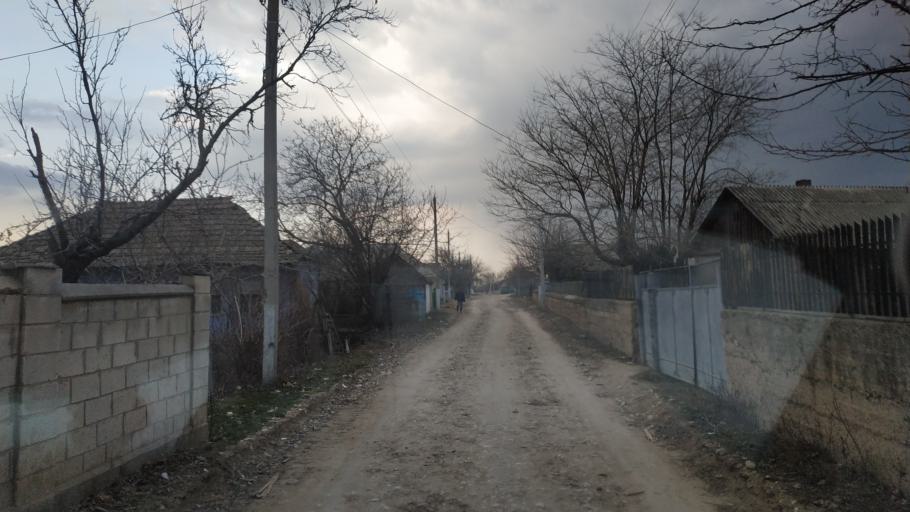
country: MD
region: Telenesti
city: Grigoriopol
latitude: 47.0231
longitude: 29.3511
